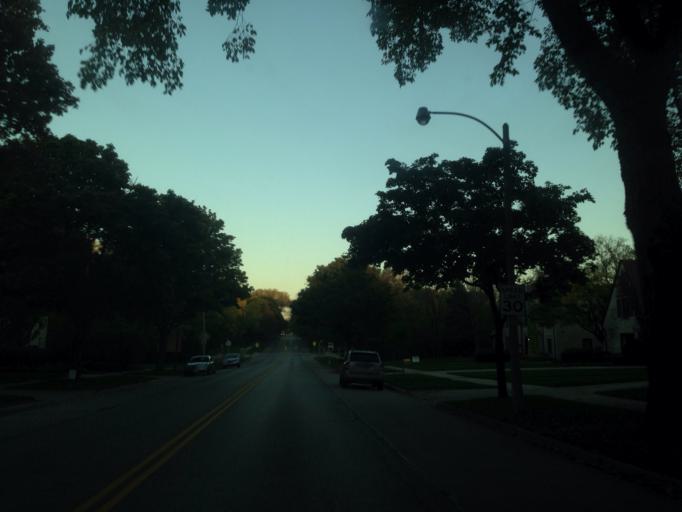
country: US
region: Wisconsin
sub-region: Milwaukee County
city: Wauwatosa
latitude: 43.0387
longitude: -88.0140
